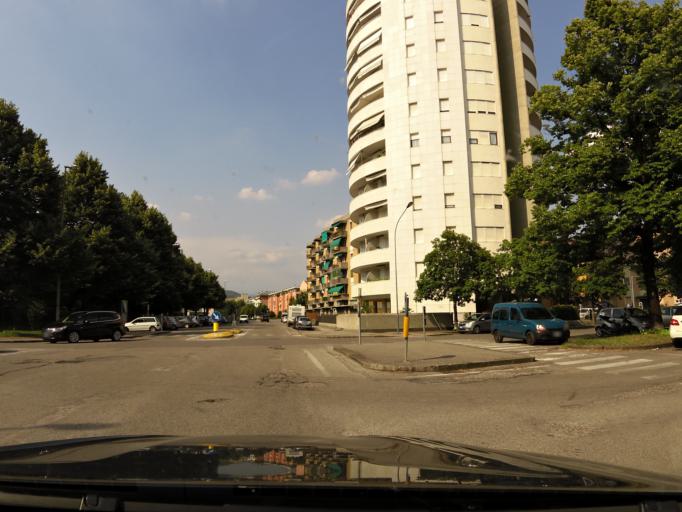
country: IT
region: Veneto
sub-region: Provincia di Verona
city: Verona
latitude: 45.4431
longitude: 10.9623
